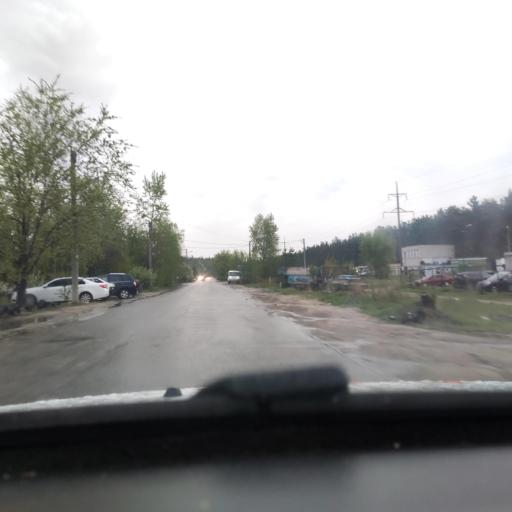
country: RU
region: Voronezj
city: Somovo
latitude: 51.7365
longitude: 39.2963
